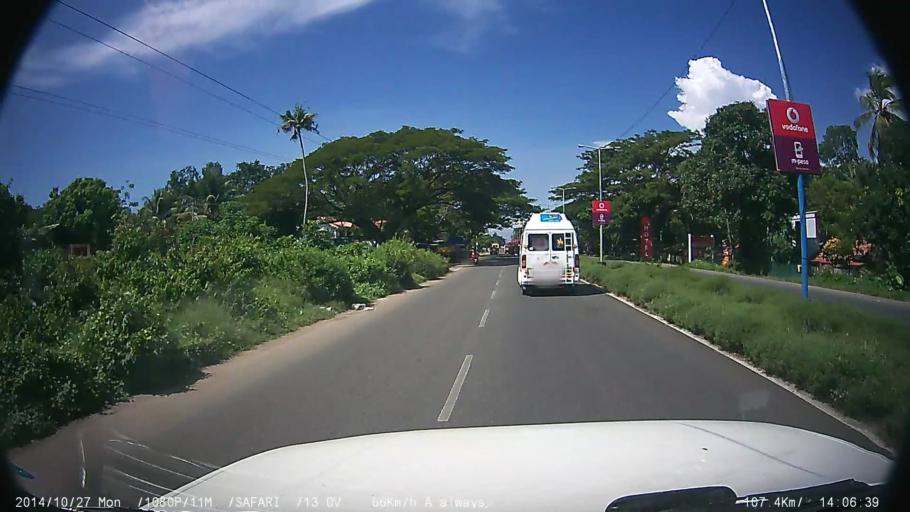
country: IN
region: Kerala
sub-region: Alappuzha
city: Kutiatodu
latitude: 9.7517
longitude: 76.3186
